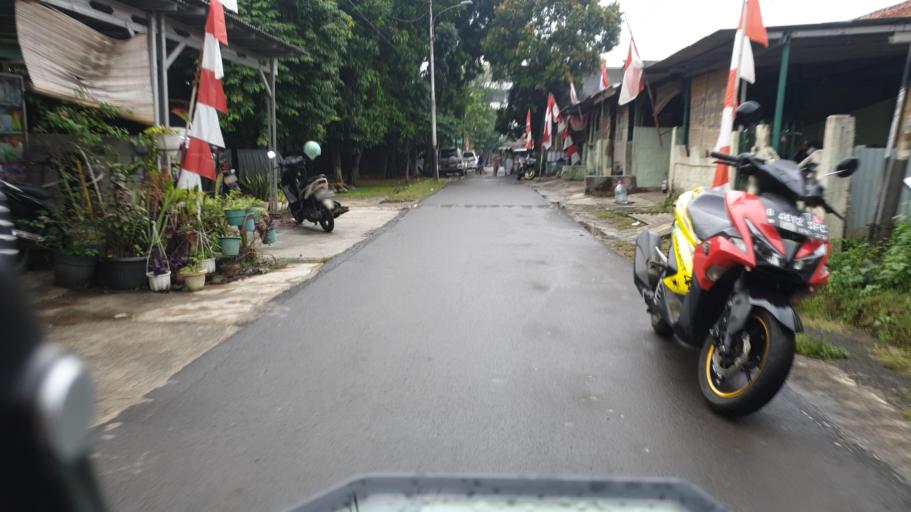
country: ID
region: West Java
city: Depok
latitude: -6.3421
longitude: 106.8317
